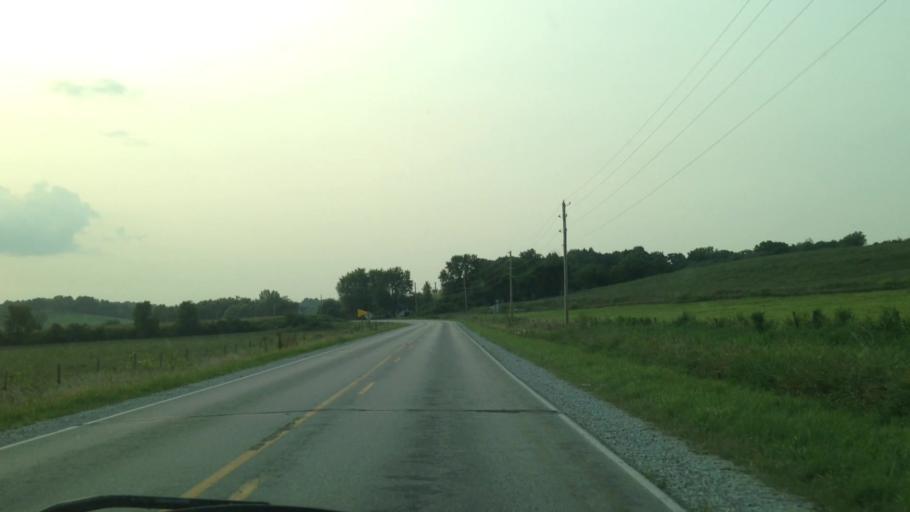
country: US
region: Iowa
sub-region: Iowa County
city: Marengo
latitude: 41.8258
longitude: -92.0717
